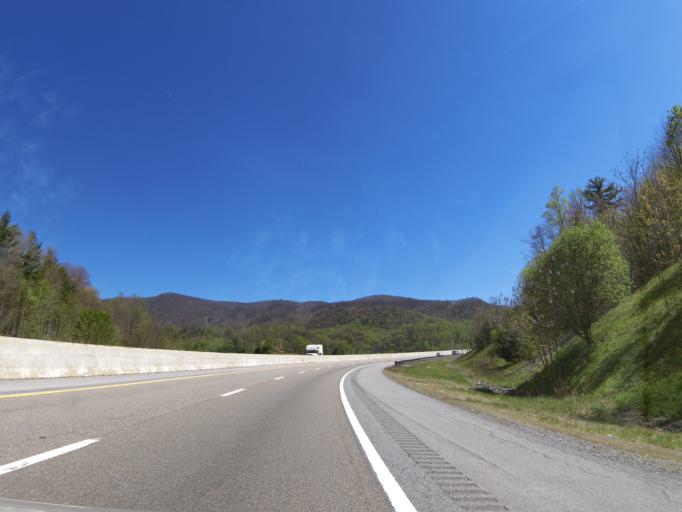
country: US
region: Tennessee
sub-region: Unicoi County
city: Banner Hill
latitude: 36.0037
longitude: -82.5412
